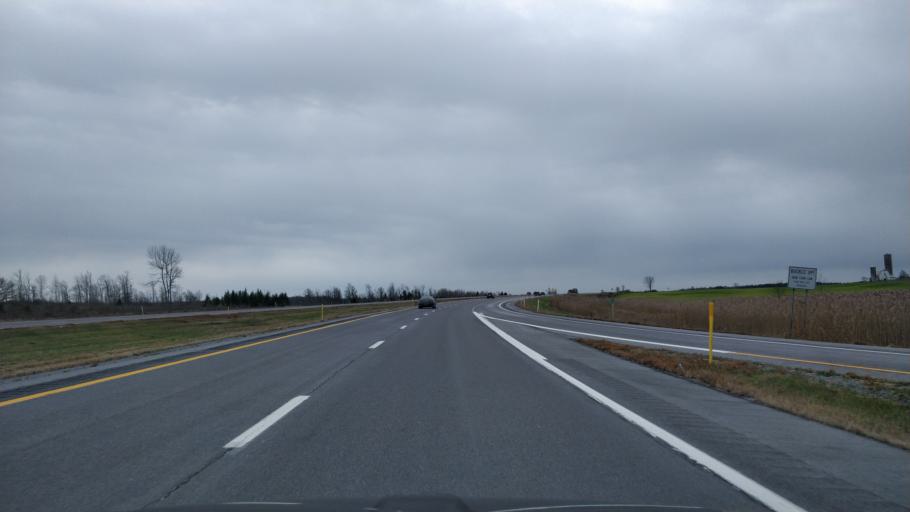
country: US
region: New York
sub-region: Jefferson County
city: Calcium
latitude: 44.1612
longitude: -75.8789
